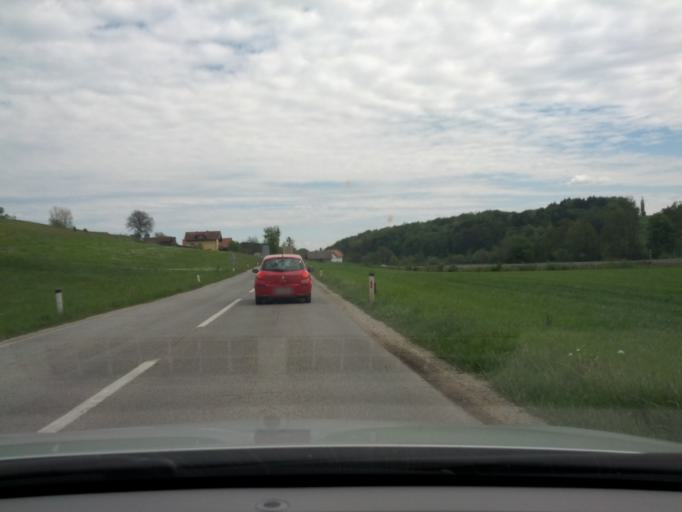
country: SI
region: Smarje pri Jelsah
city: Smarje pri Jelsah
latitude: 46.2337
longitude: 15.5362
